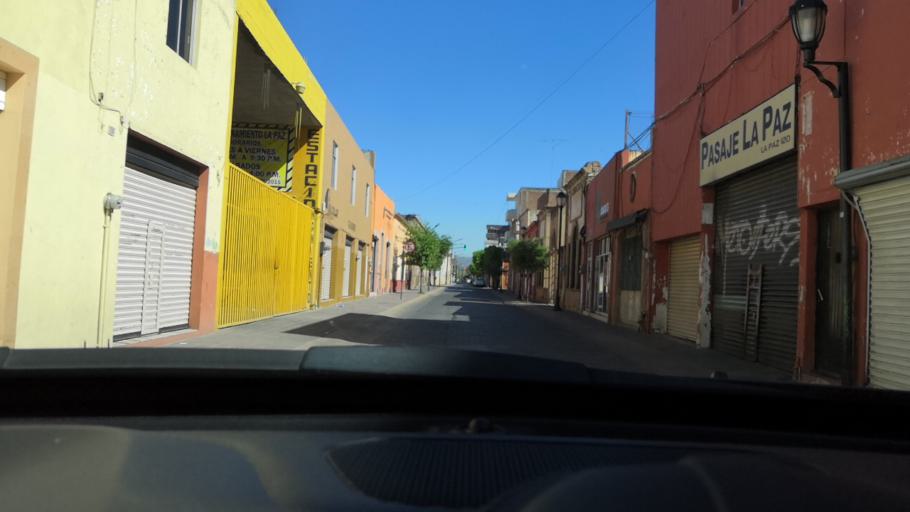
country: MX
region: Guanajuato
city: Leon
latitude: 21.1217
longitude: -101.6785
